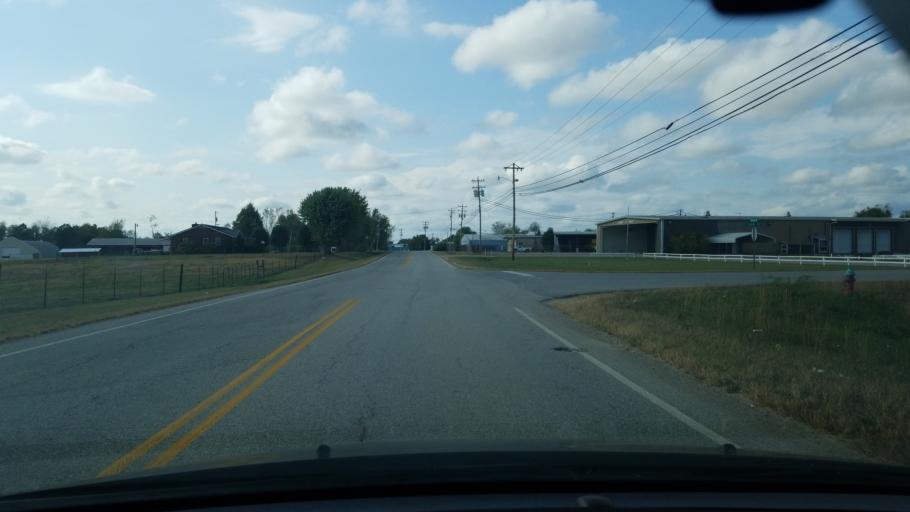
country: US
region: Tennessee
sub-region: Cumberland County
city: Crossville
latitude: 35.9754
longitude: -85.0173
